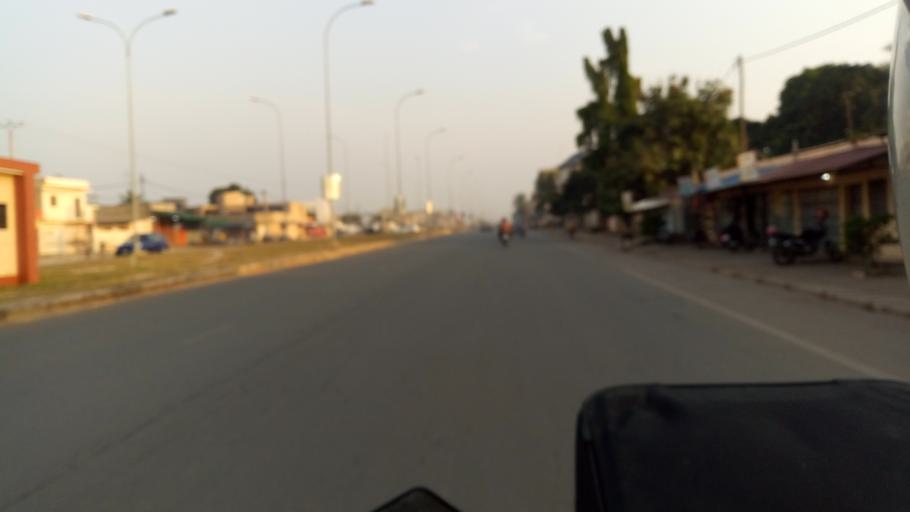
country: TG
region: Maritime
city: Lome
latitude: 6.2024
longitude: 1.1817
